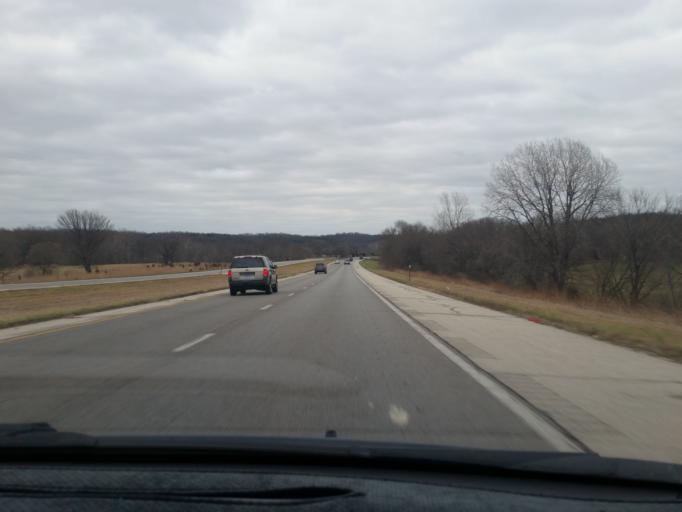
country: US
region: Kansas
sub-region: Johnson County
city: De Soto
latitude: 38.9576
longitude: -94.9211
